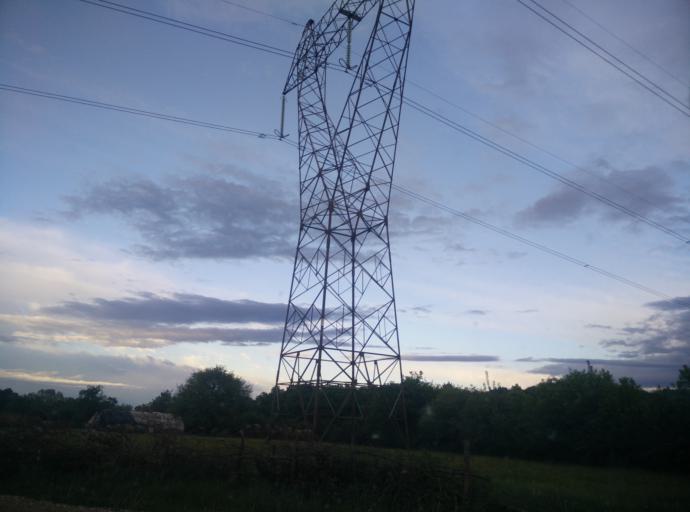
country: BA
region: Brcko
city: Brcko
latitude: 44.7798
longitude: 18.8341
